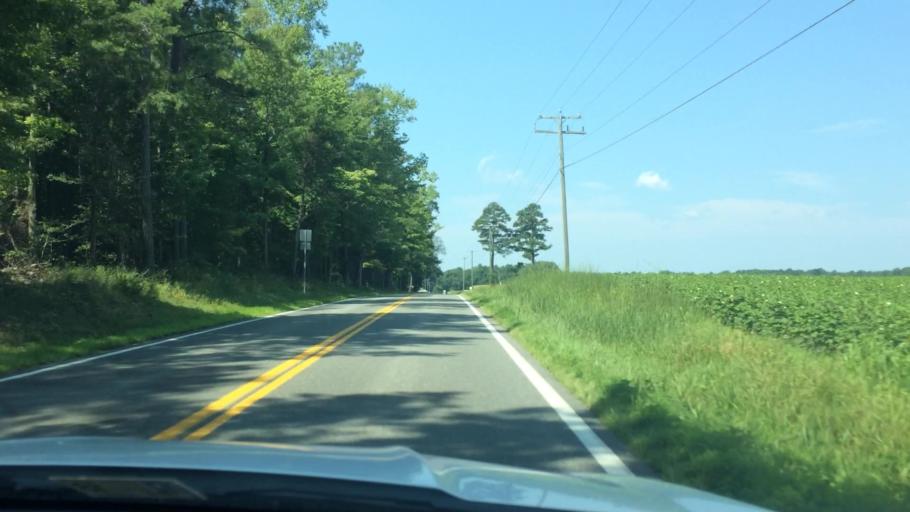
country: US
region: Virginia
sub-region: New Kent County
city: New Kent
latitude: 37.5256
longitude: -77.0392
